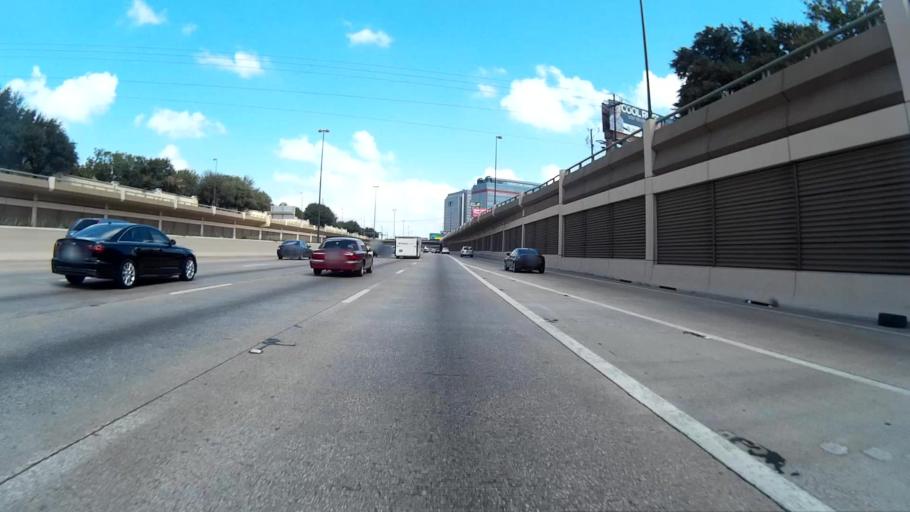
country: US
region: Texas
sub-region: Dallas County
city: Highland Park
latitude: 32.8421
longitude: -96.7751
